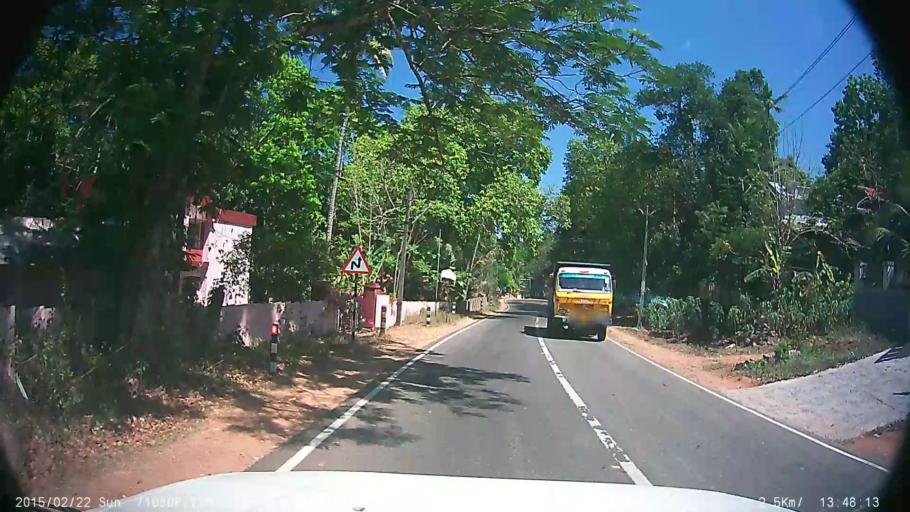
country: IN
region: Kerala
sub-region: Kottayam
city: Changanacheri
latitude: 9.4943
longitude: 76.6260
